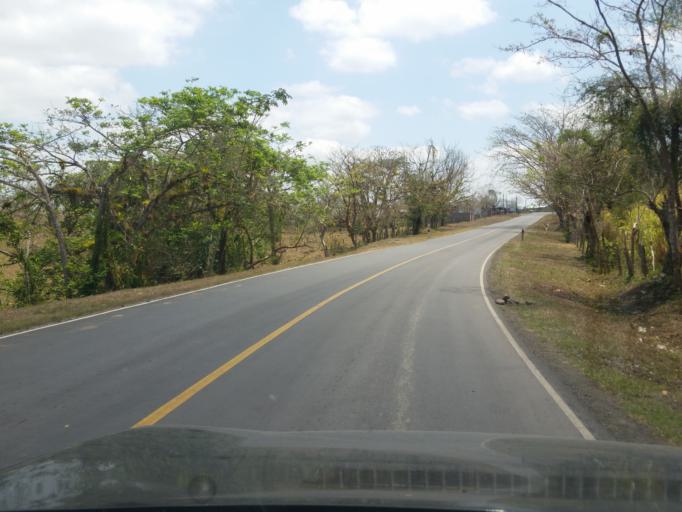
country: NI
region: Matagalpa
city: Muy Muy
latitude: 12.6170
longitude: -85.5373
